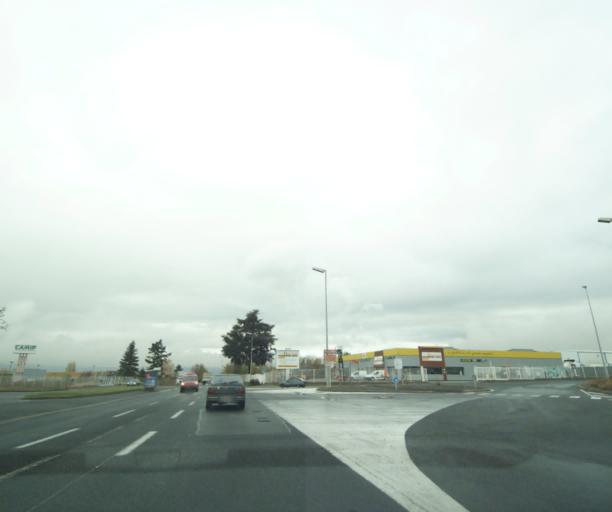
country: FR
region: Auvergne
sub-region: Departement du Puy-de-Dome
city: Perignat-les-Sarlieve
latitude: 45.7460
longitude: 3.1641
